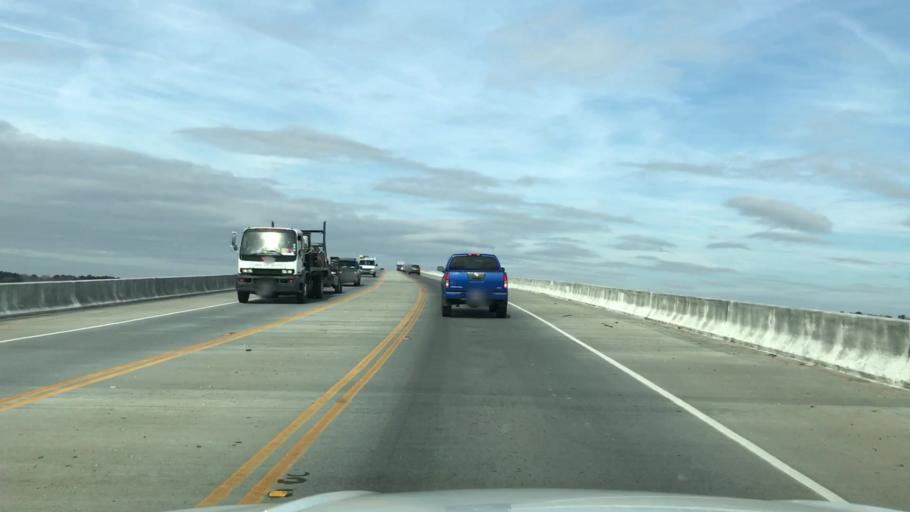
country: US
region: South Carolina
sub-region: Charleston County
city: Shell Point
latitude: 32.7819
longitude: -80.1061
